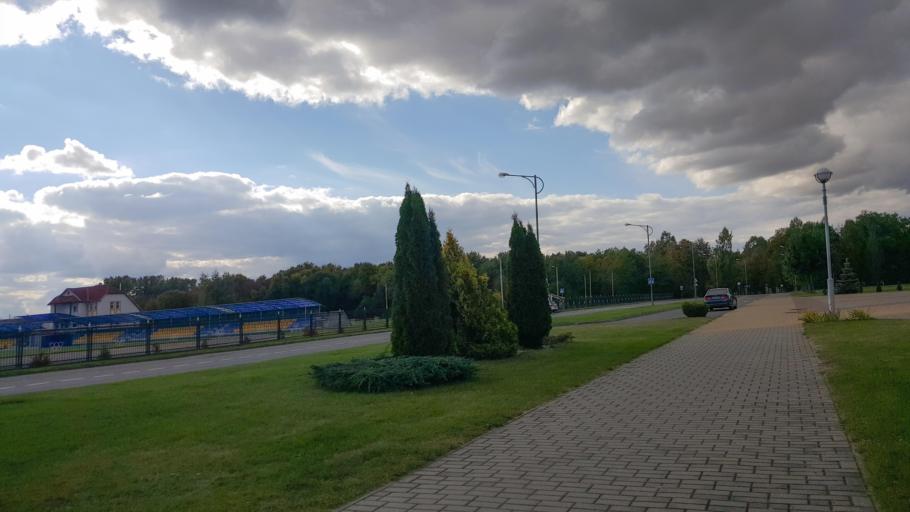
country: BY
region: Brest
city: Kamyanyets
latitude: 52.3995
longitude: 23.8124
